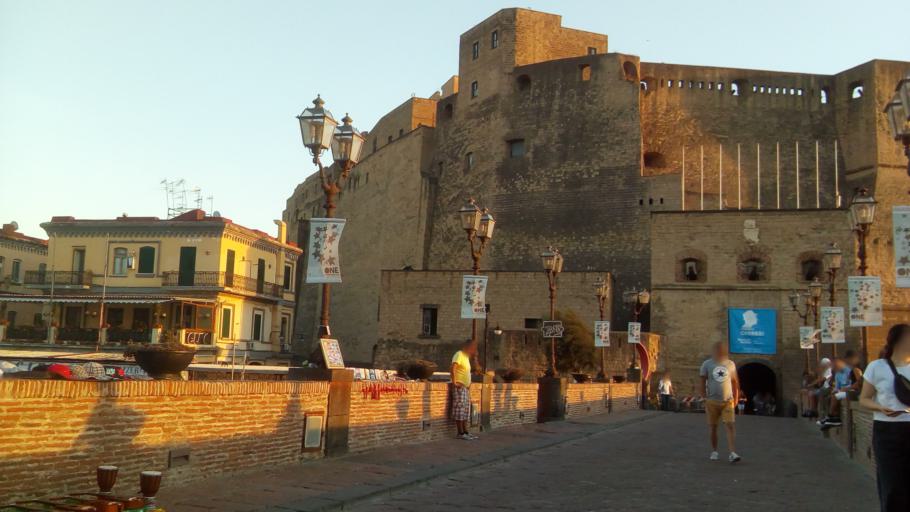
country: IT
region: Campania
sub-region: Provincia di Napoli
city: Napoli
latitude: 40.8301
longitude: 14.2468
